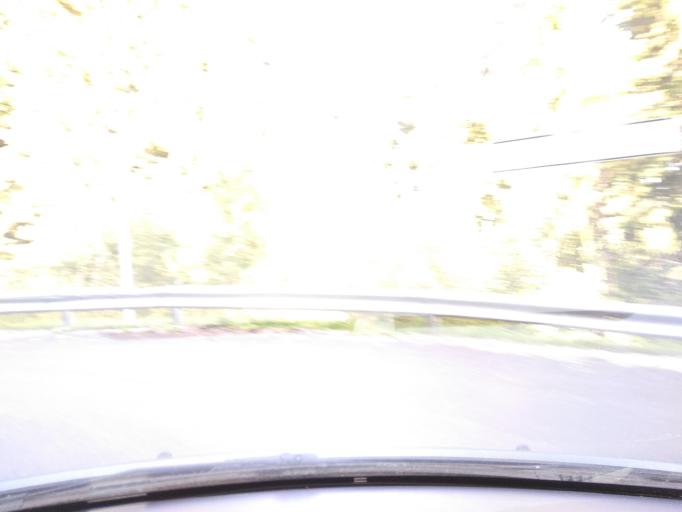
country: FR
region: Rhone-Alpes
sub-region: Departement de la Savoie
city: Beaufort
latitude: 45.7704
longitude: 6.5332
